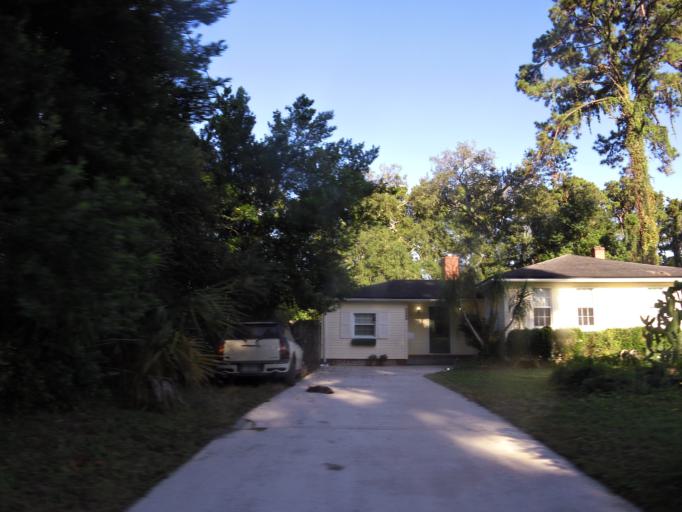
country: US
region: Florida
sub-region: Duval County
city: Jacksonville
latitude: 30.2681
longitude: -81.6401
